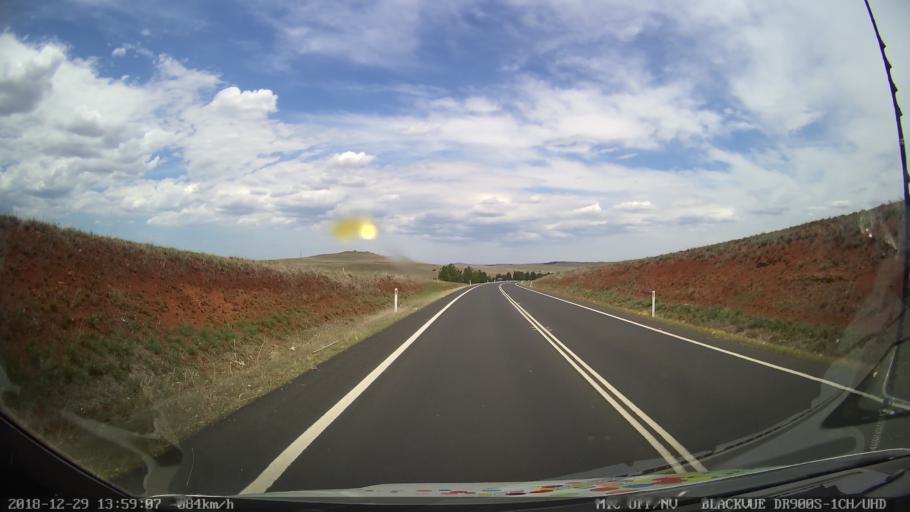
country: AU
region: New South Wales
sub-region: Cooma-Monaro
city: Cooma
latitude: -36.2486
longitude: 149.1465
